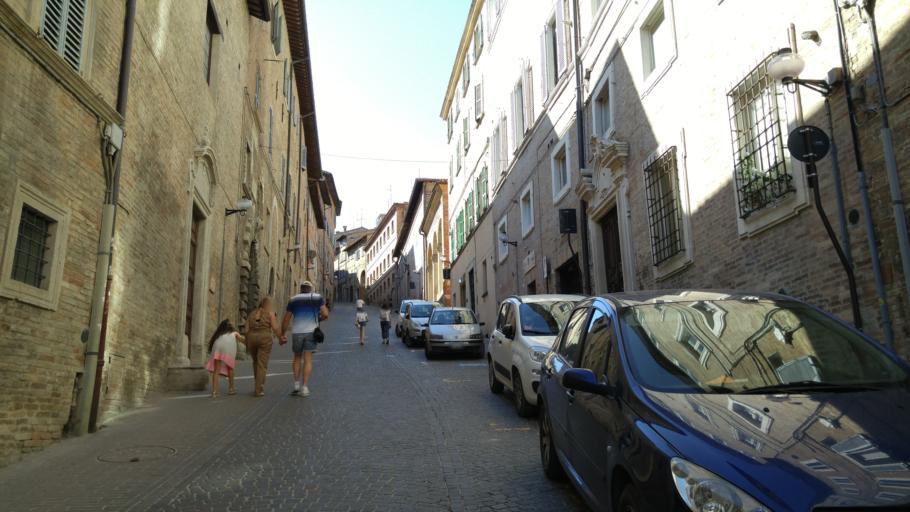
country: IT
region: The Marches
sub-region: Provincia di Pesaro e Urbino
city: Urbino
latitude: 43.7272
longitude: 12.6354
